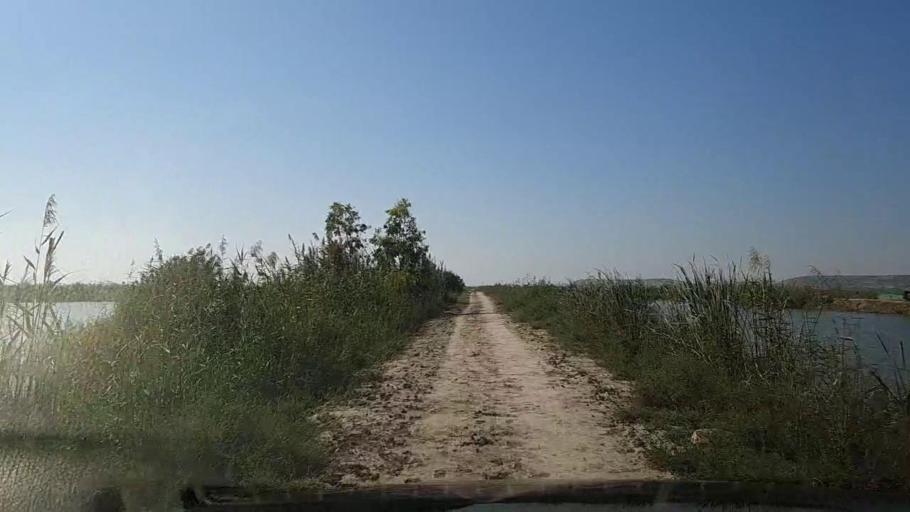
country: PK
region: Sindh
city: Thatta
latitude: 24.6901
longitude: 67.8938
